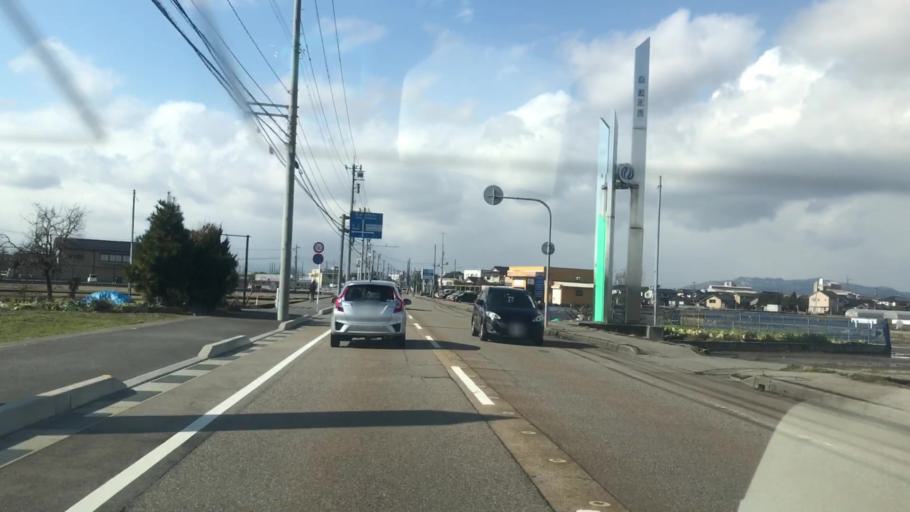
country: JP
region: Toyama
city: Takaoka
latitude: 36.7270
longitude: 137.0621
